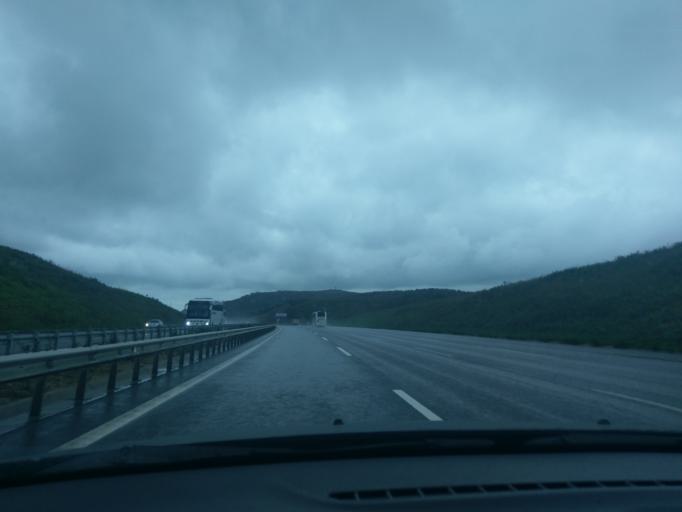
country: TR
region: Istanbul
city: Arikoey
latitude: 41.2304
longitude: 28.9346
